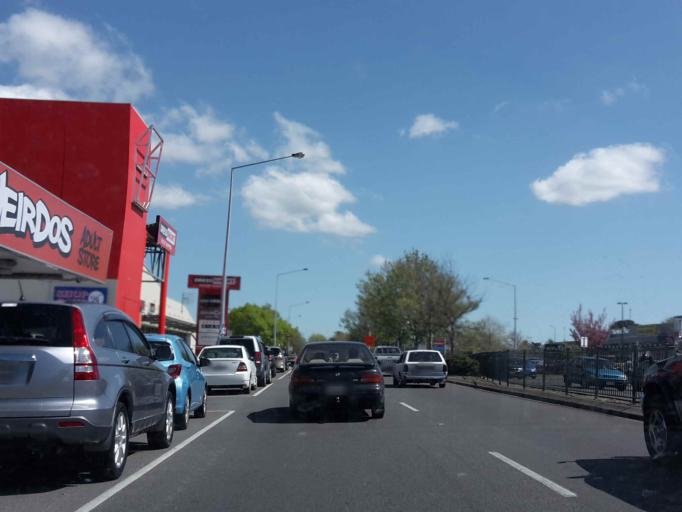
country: NZ
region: Canterbury
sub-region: Selwyn District
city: Prebbleton
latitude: -43.5435
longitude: 172.5253
